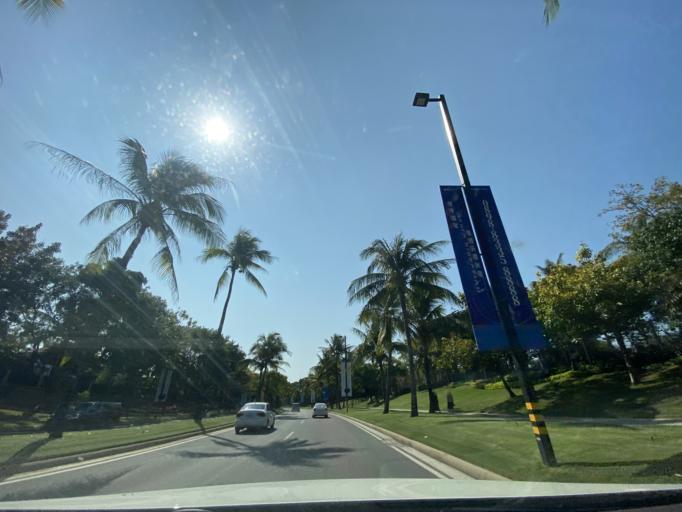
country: CN
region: Hainan
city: Yingzhou
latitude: 18.4008
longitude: 109.8500
